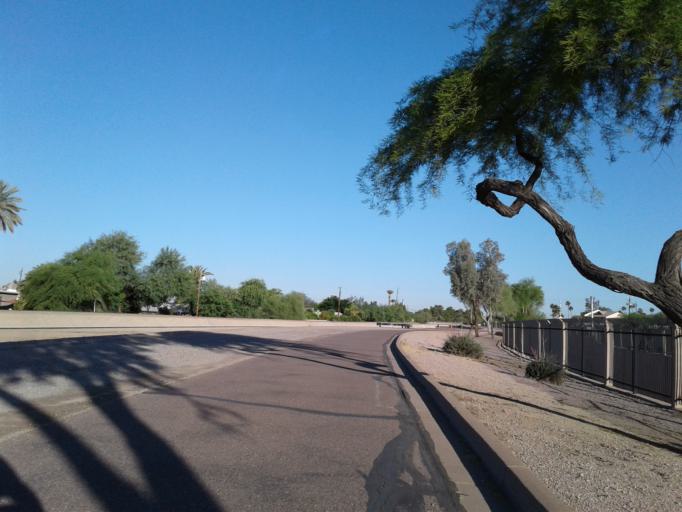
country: US
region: Arizona
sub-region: Maricopa County
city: Phoenix
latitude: 33.5439
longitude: -112.0531
